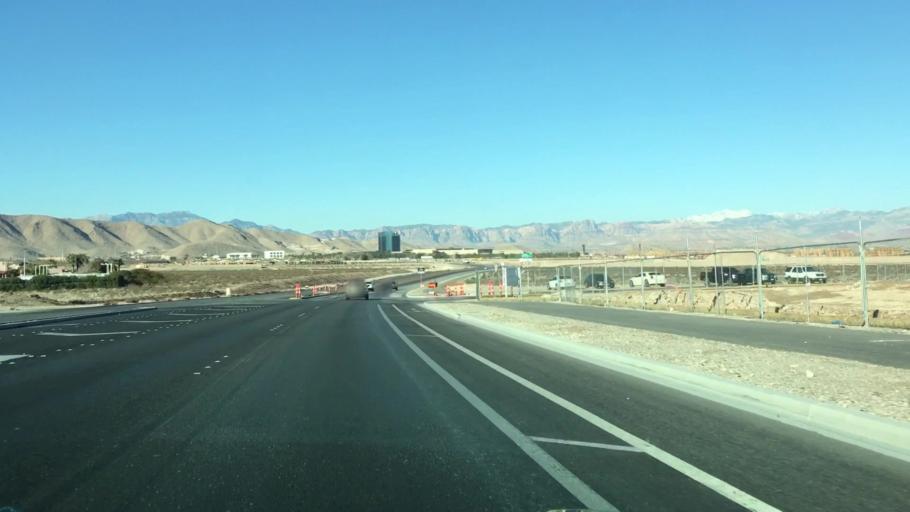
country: US
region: Nevada
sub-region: Clark County
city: Enterprise
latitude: 35.9604
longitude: -115.1496
